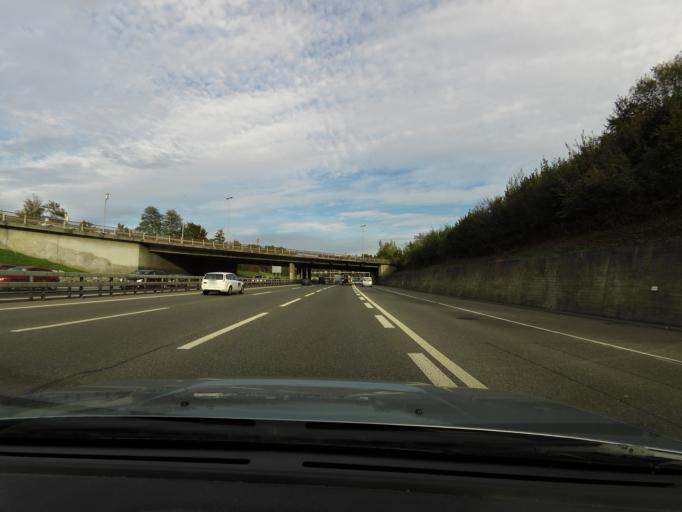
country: CH
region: Aargau
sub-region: Bezirk Baden
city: Birmenstorf
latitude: 47.4574
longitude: 8.2779
